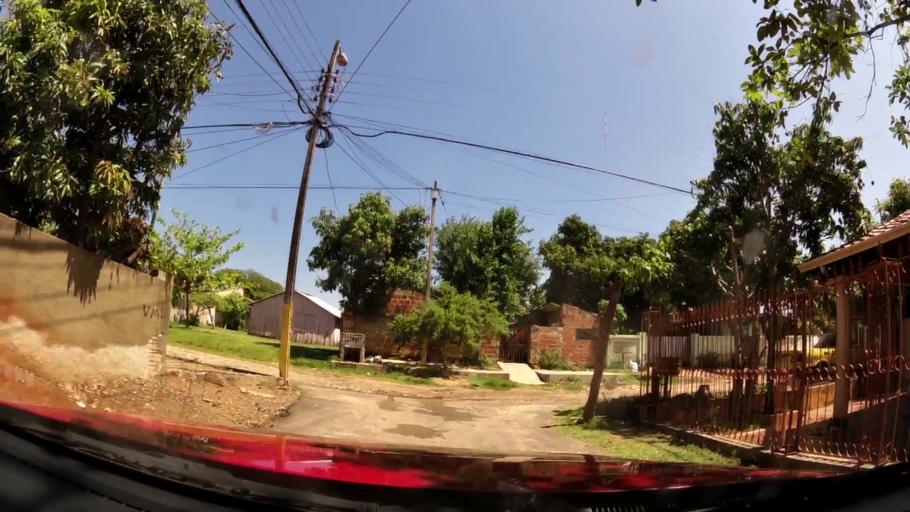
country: PY
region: Central
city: Colonia Mariano Roque Alonso
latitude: -25.2469
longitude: -57.5546
